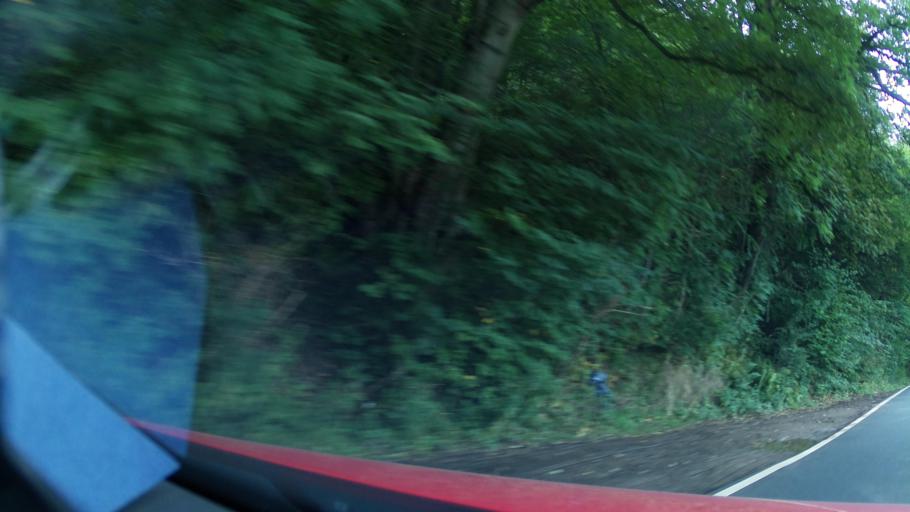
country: GB
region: England
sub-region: North Yorkshire
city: Leyburn
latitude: 54.4014
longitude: -1.8236
